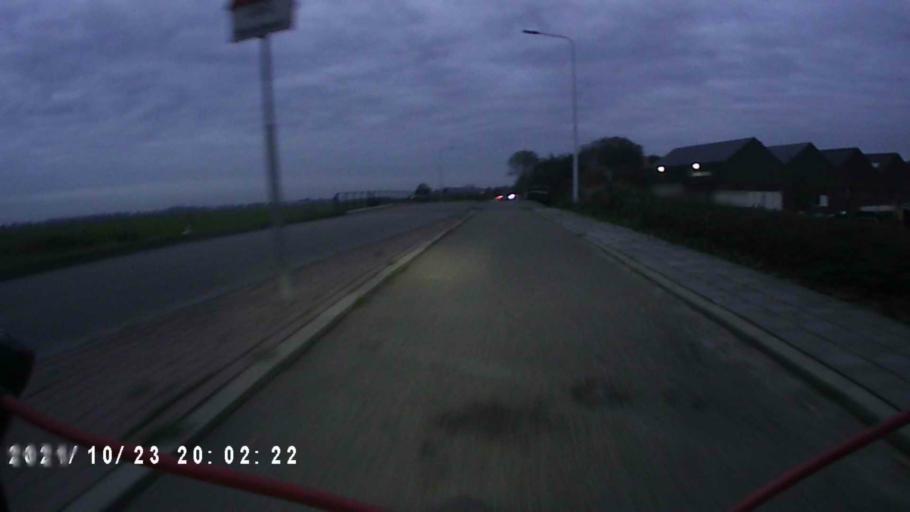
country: NL
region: Friesland
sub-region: Sudwest Fryslan
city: Bolsward
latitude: 53.1047
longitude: 5.4665
